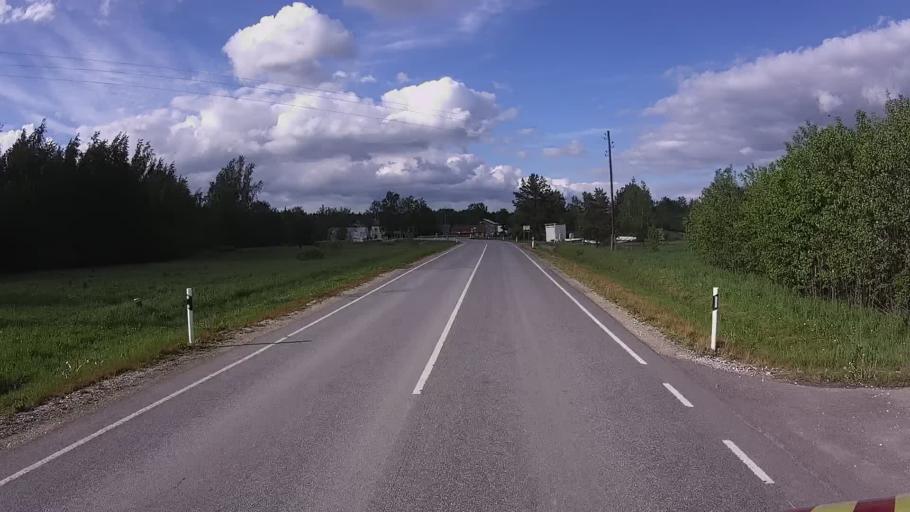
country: EE
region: Jogevamaa
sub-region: Mustvee linn
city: Mustvee
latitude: 58.9778
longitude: 26.8283
